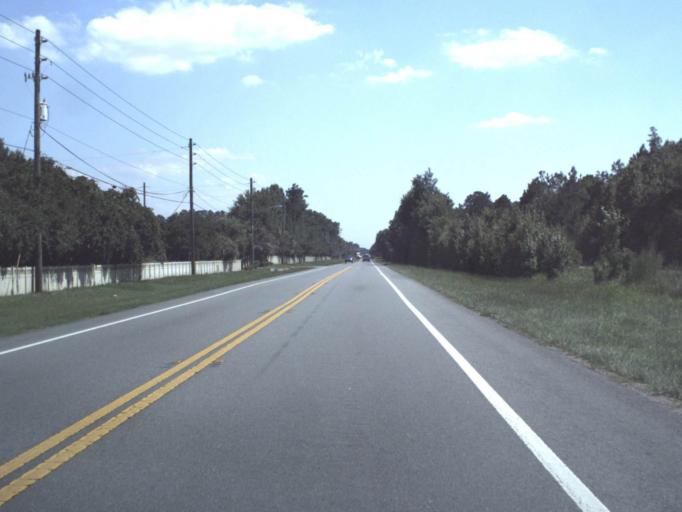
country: US
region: Florida
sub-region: Nassau County
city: Yulee
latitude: 30.5252
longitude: -81.6224
